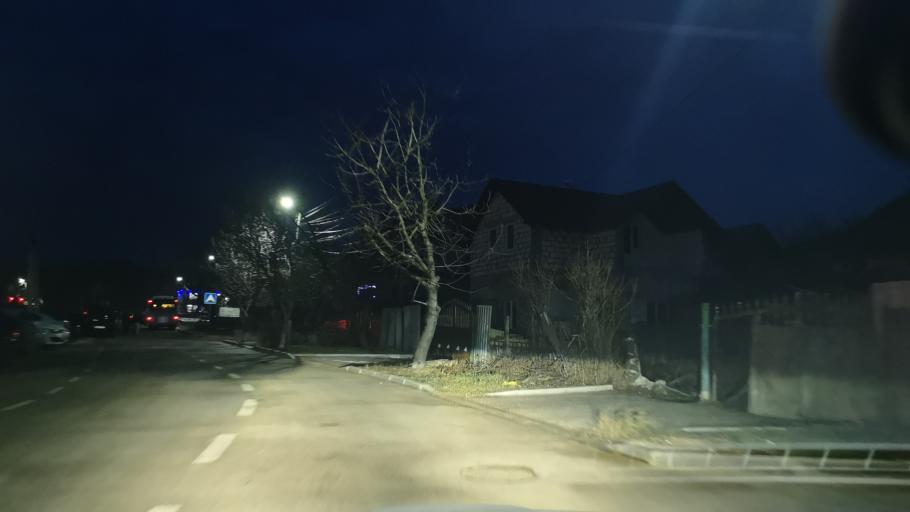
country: MD
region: Orhei
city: Orhei
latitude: 47.3883
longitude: 28.8308
